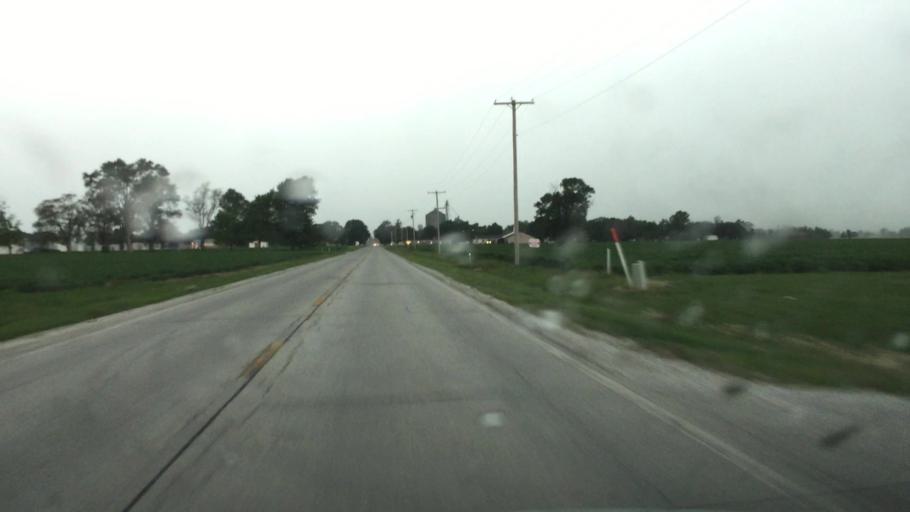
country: US
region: Illinois
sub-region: Adams County
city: Camp Point
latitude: 40.2314
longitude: -91.0501
